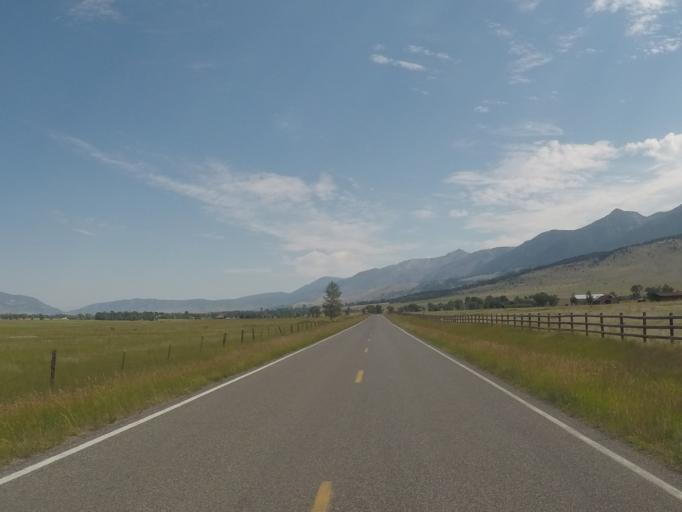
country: US
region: Montana
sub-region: Park County
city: Livingston
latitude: 45.4275
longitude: -110.6196
